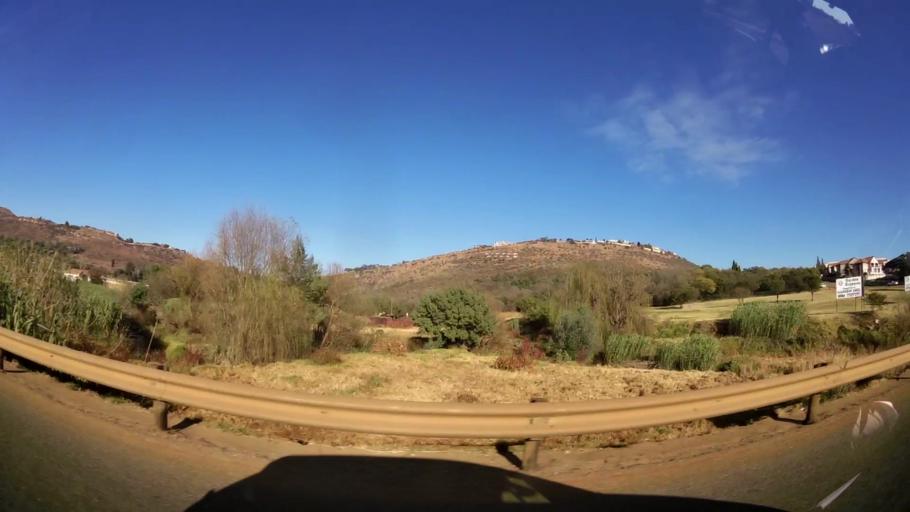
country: ZA
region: Gauteng
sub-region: City of Johannesburg Metropolitan Municipality
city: Roodepoort
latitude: -26.1073
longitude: 27.8822
